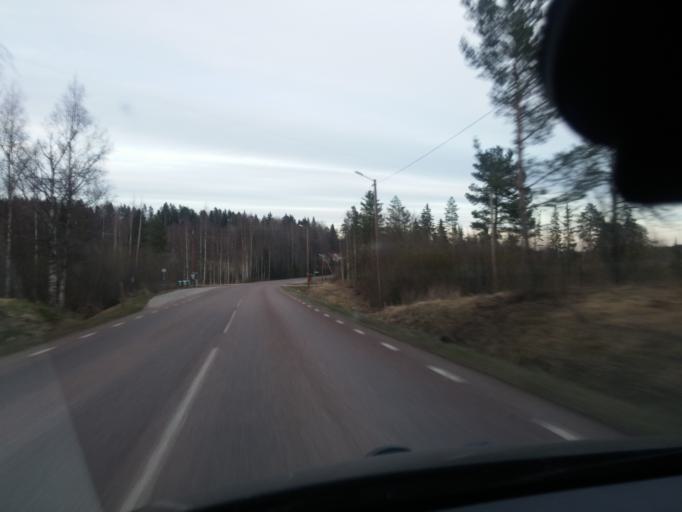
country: SE
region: Dalarna
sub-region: Faluns Kommun
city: Bjursas
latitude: 60.7192
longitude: 15.3316
